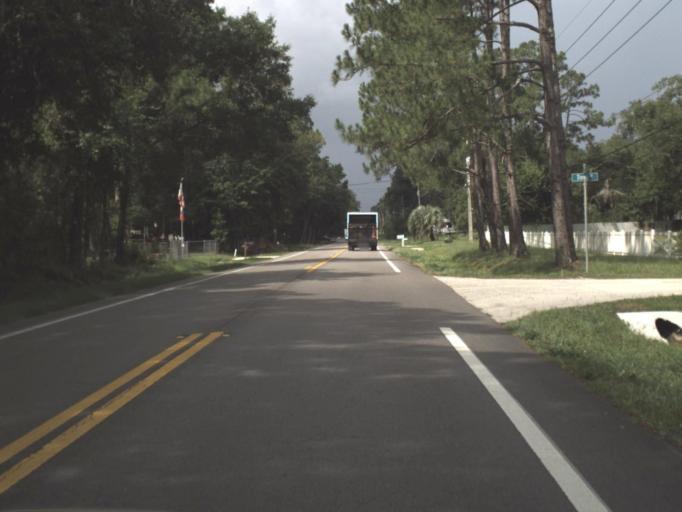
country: US
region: Florida
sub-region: Saint Johns County
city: Fruit Cove
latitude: 30.0710
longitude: -81.6538
